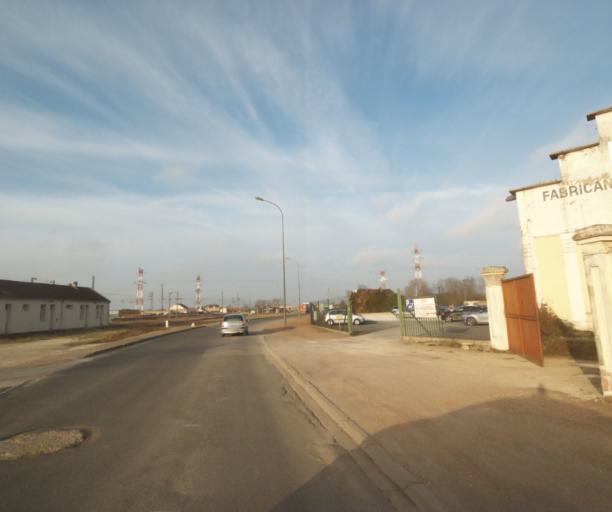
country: FR
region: Champagne-Ardenne
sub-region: Departement de la Haute-Marne
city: Saint-Dizier
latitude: 48.6456
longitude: 4.9393
